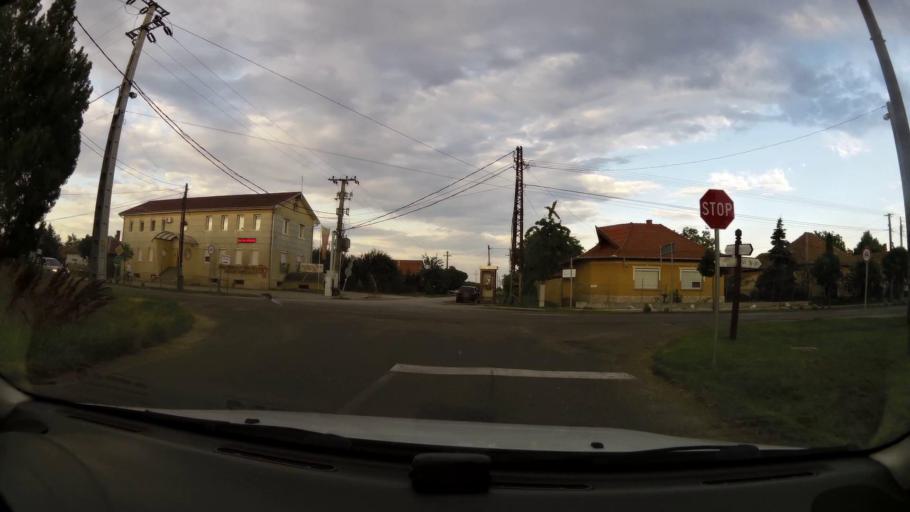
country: HU
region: Pest
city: Tapioszele
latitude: 47.3200
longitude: 19.8749
